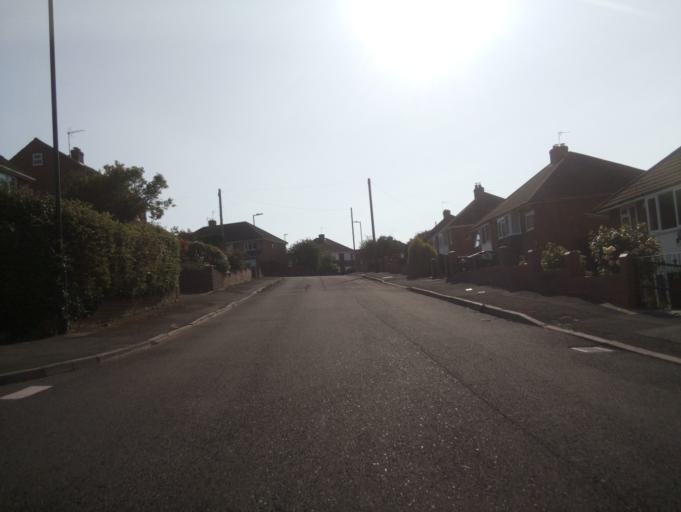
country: GB
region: England
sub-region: Gloucestershire
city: Dursley
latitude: 51.6973
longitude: -2.3657
